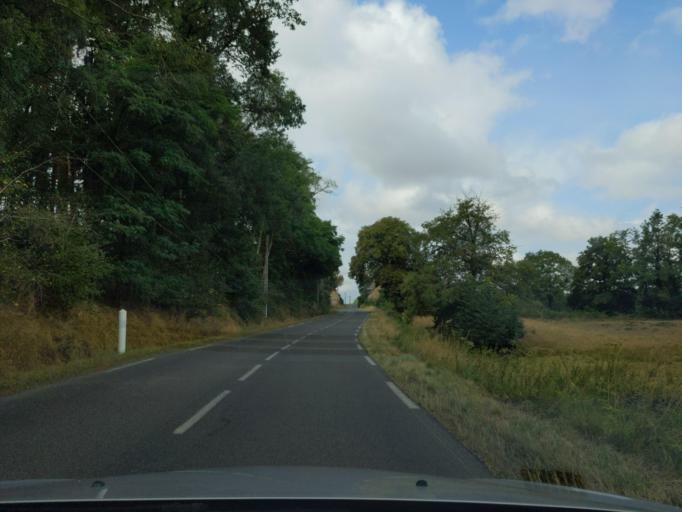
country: FR
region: Bourgogne
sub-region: Departement de la Nievre
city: Luzy
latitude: 46.7263
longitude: 3.9142
